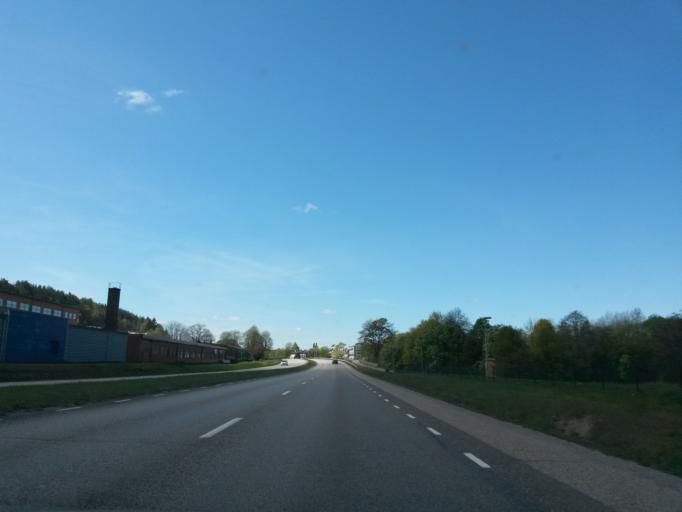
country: SE
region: Vaestra Goetaland
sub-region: Alingsas Kommun
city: Alingsas
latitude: 57.9299
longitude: 12.5570
